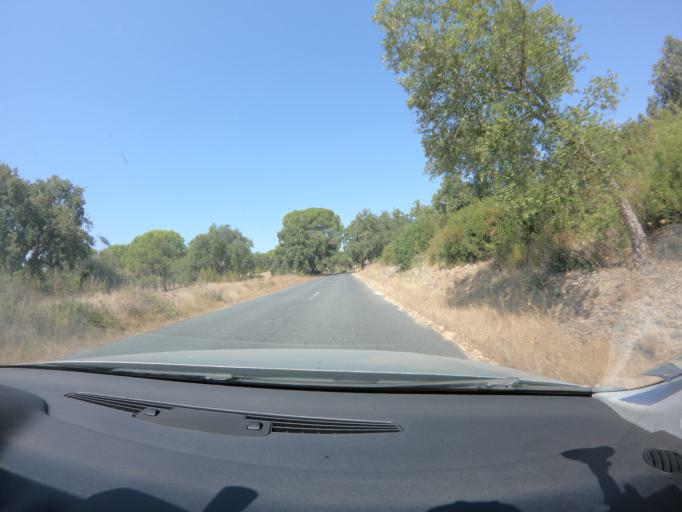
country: PT
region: Setubal
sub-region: Alcacer do Sal
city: Alcacer do Sal
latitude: 38.3025
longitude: -8.4063
